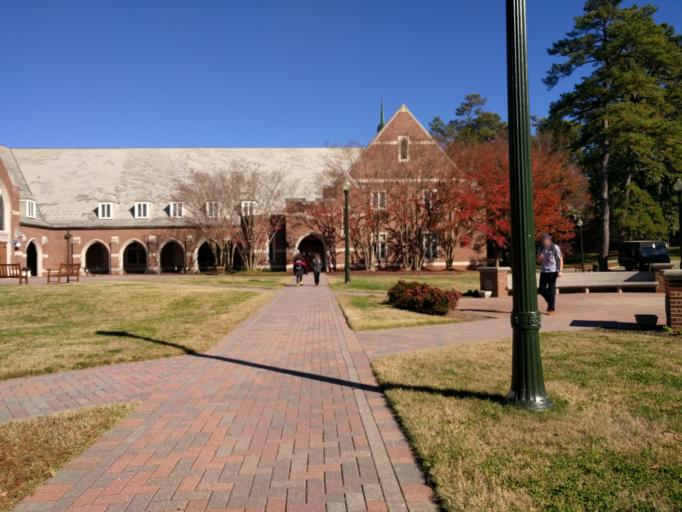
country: US
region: Virginia
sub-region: Henrico County
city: Tuckahoe
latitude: 37.5778
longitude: -77.5374
